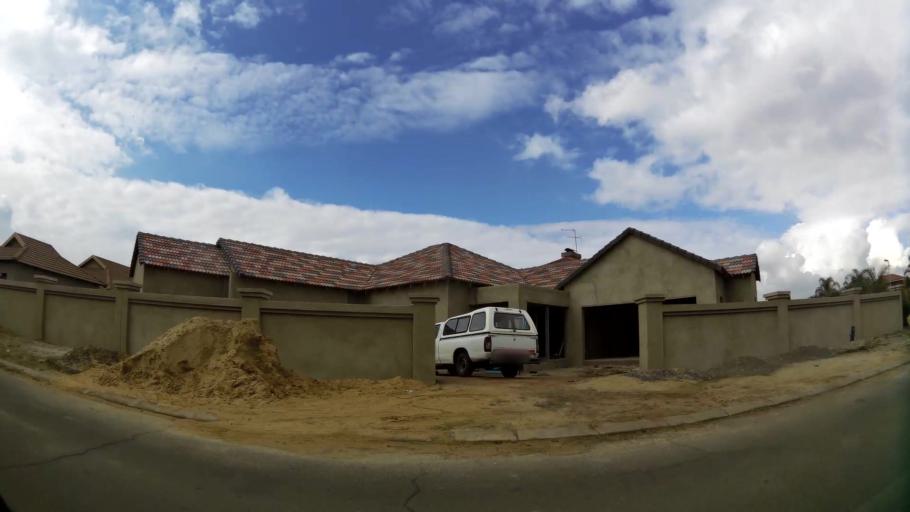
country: ZA
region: Gauteng
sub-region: Sedibeng District Municipality
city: Vanderbijlpark
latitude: -26.7264
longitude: 27.8675
